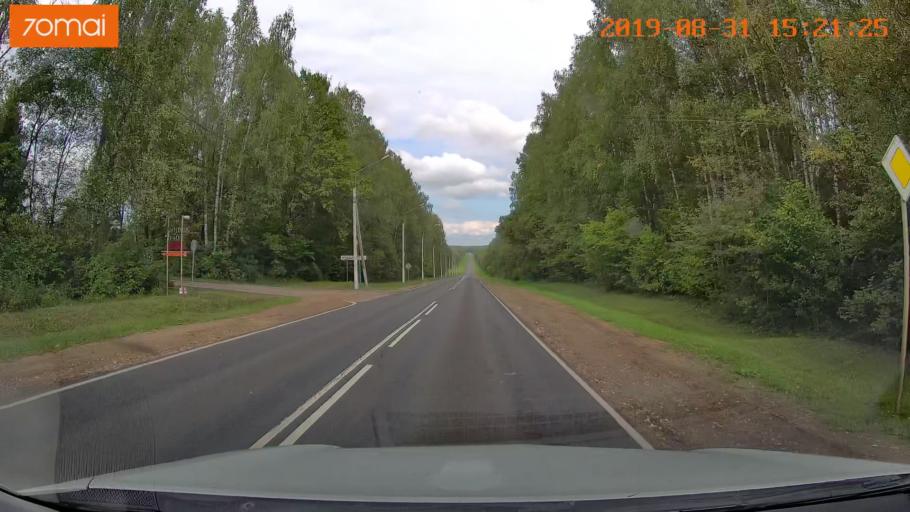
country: RU
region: Kaluga
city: Baryatino
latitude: 54.4960
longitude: 34.4530
